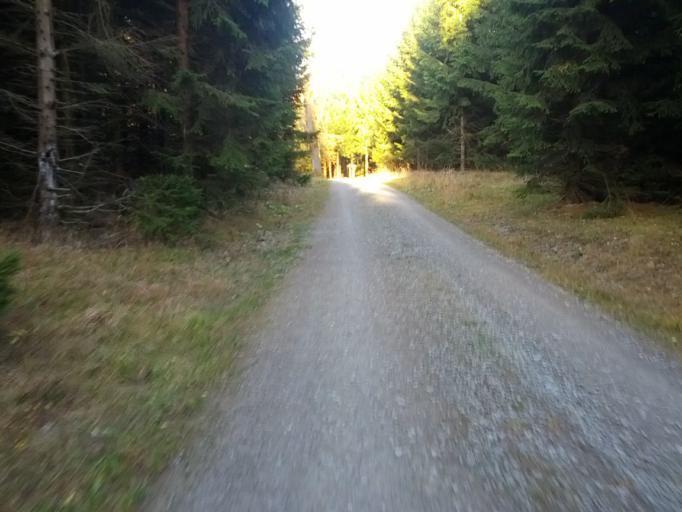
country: DE
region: Thuringia
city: Seebach
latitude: 50.8952
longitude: 10.4299
